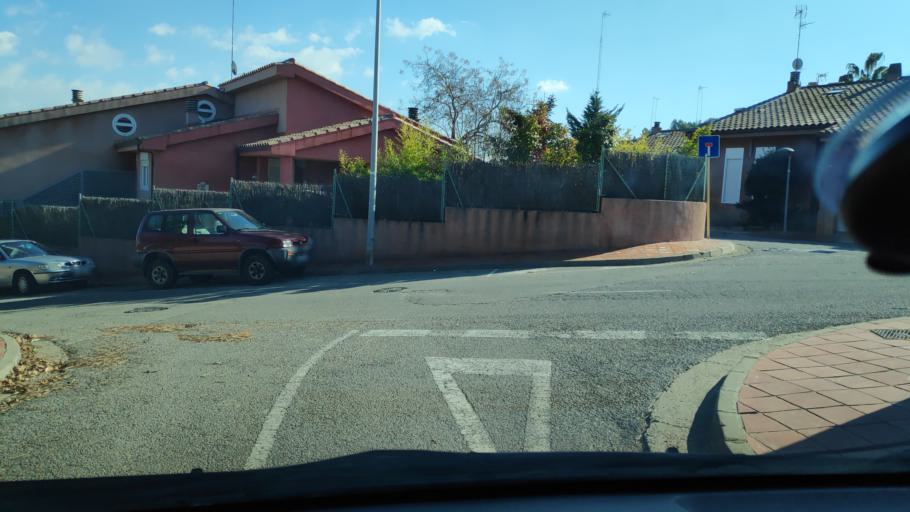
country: ES
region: Catalonia
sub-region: Provincia de Barcelona
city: Sant Quirze del Valles
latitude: 41.5249
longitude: 2.0708
